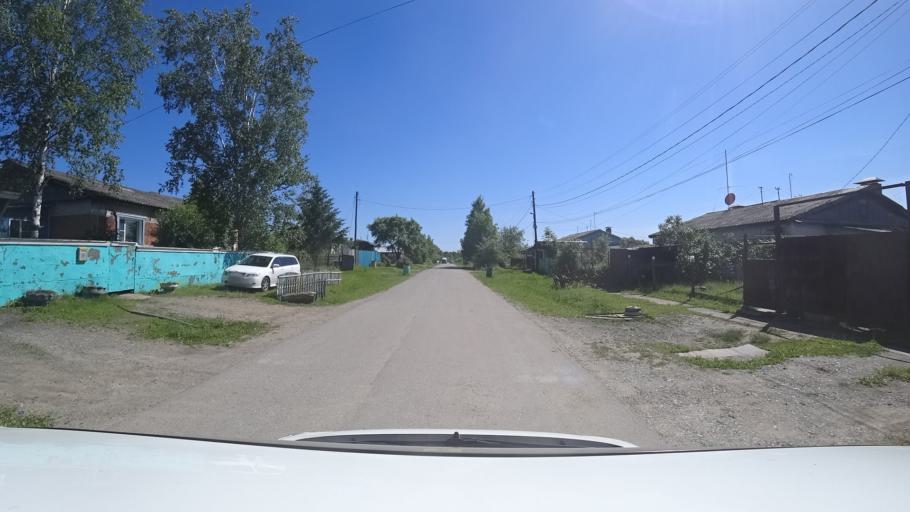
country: RU
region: Khabarovsk Krai
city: Topolevo
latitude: 48.5585
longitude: 135.1906
